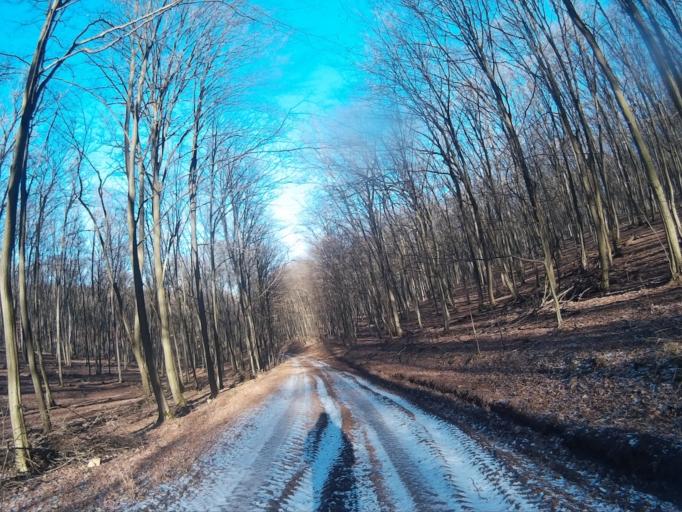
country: HU
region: Borsod-Abauj-Zemplen
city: Rudabanya
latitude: 48.5077
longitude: 20.6060
